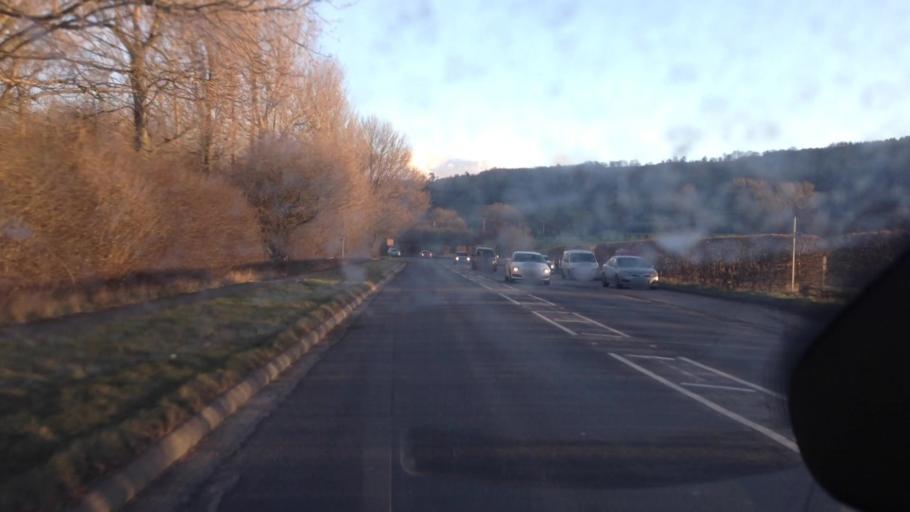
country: GB
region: England
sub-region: City and Borough of Leeds
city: Otley
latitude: 53.9074
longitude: -1.6585
